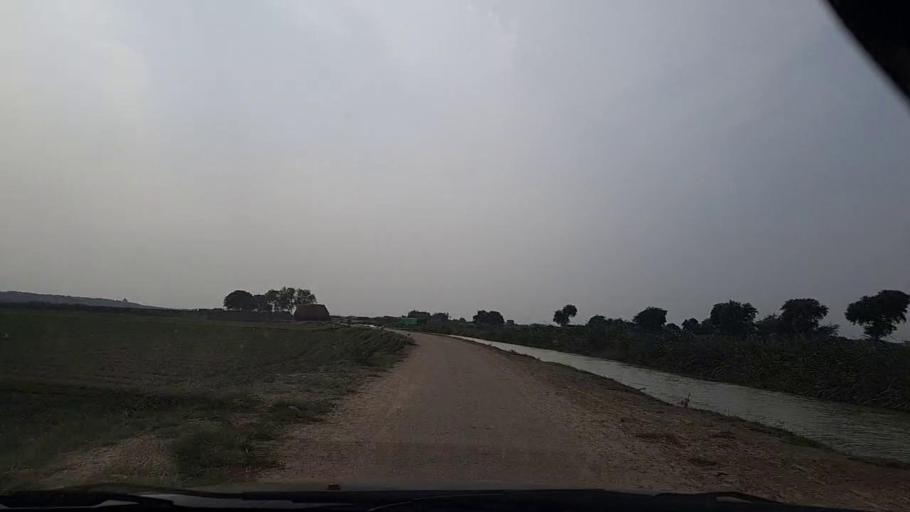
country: PK
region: Sindh
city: Thatta
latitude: 24.5754
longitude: 67.8810
